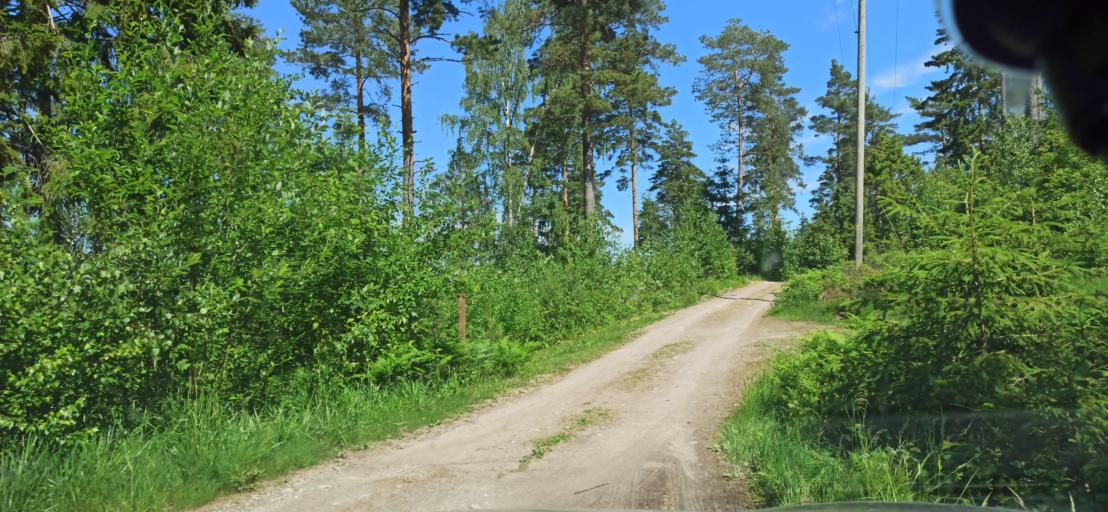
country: FI
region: Varsinais-Suomi
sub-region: Turku
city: Sauvo
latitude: 60.3818
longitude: 22.6207
